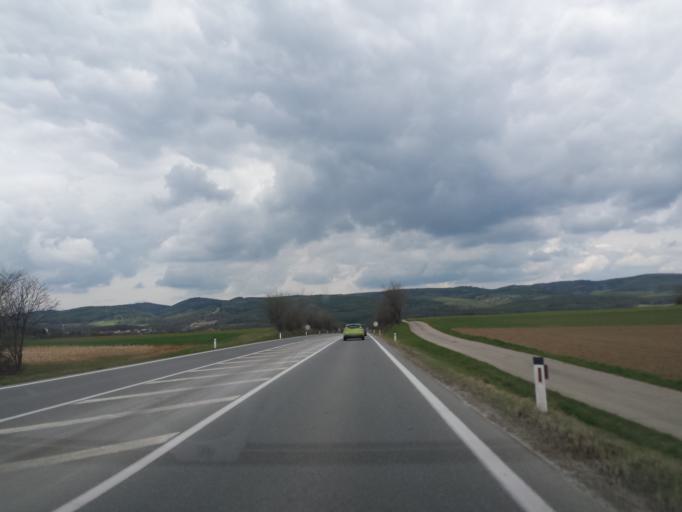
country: AT
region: Lower Austria
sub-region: Politischer Bezirk Krems
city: Stratzing
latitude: 48.4596
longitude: 15.5947
